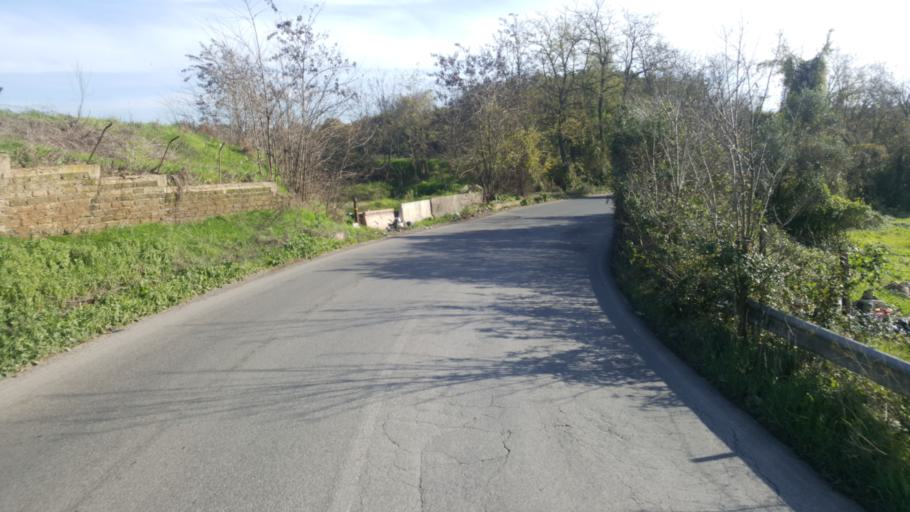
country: IT
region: Latium
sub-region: Citta metropolitana di Roma Capitale
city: Mantiglia di Ardea
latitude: 41.6892
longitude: 12.6027
